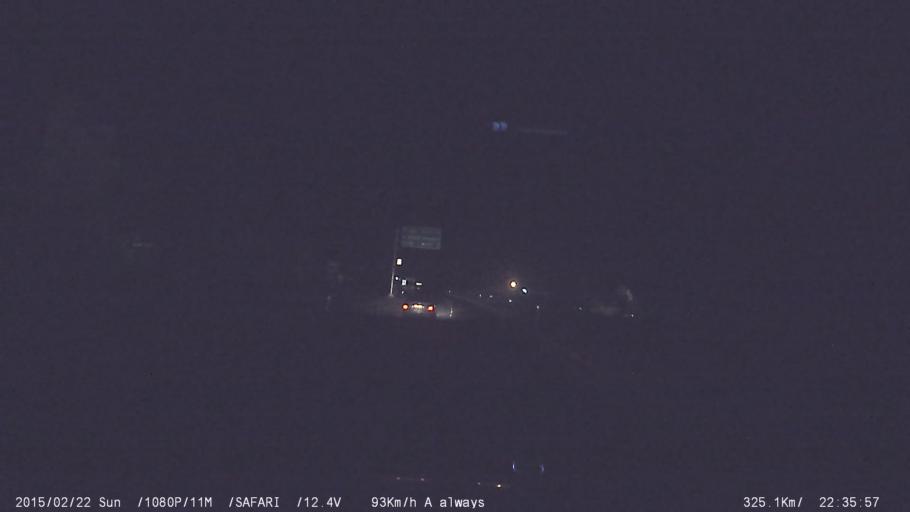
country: IN
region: Tamil Nadu
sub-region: Namakkal
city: Velur
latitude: 11.1401
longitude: 78.0204
